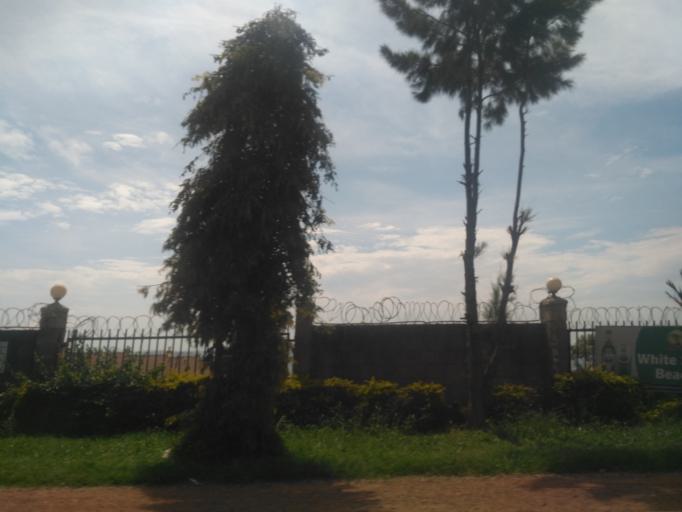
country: UG
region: Central Region
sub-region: Wakiso District
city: Entebbe
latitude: 0.0368
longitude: 32.4568
